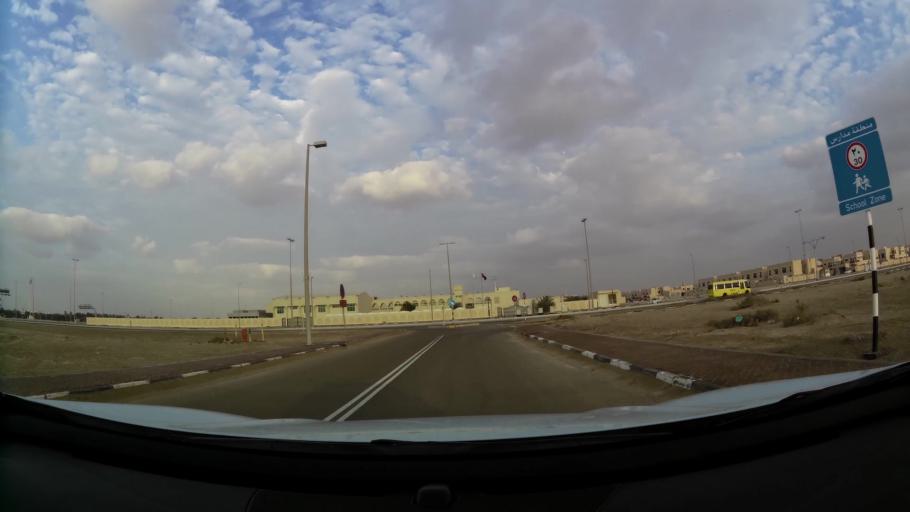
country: AE
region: Abu Dhabi
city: Abu Dhabi
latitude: 24.3817
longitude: 54.5353
